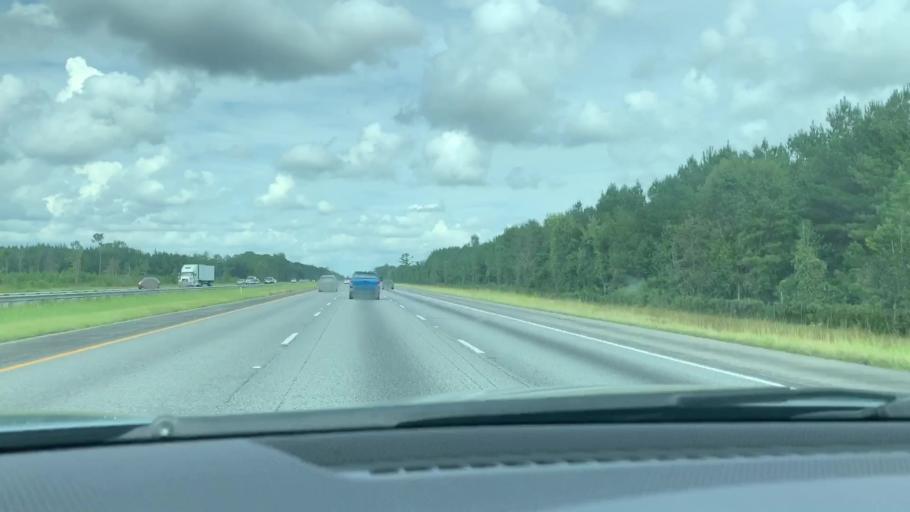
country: US
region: Georgia
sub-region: Liberty County
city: Midway
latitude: 31.6137
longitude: -81.4147
